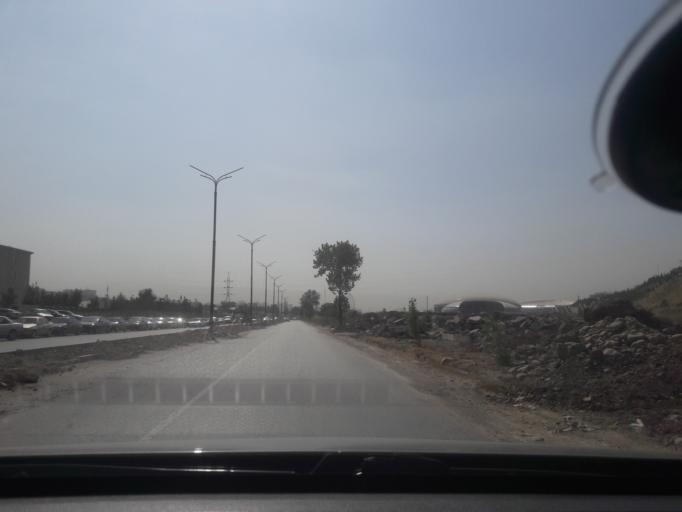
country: TJ
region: Dushanbe
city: Dushanbe
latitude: 38.6075
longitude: 68.7717
